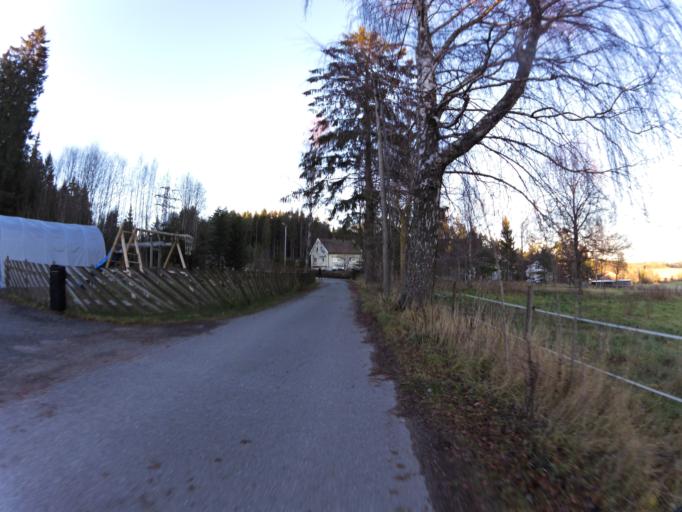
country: NO
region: Ostfold
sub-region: Fredrikstad
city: Fredrikstad
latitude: 59.2433
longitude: 10.9641
